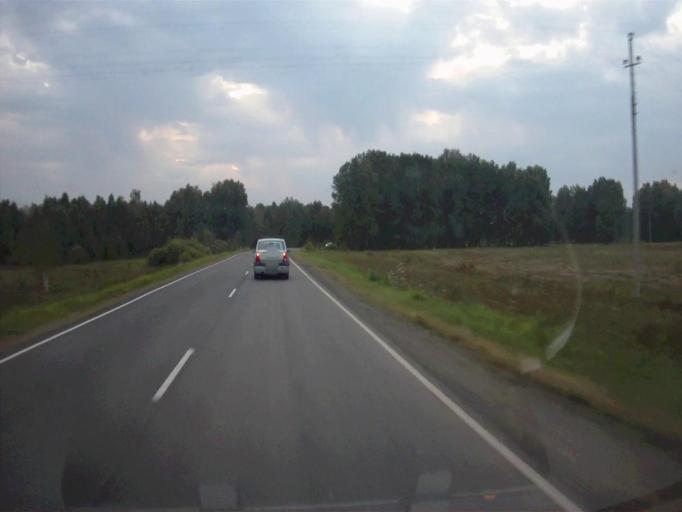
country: RU
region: Chelyabinsk
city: Chebarkul'
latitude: 55.1831
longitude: 60.4715
